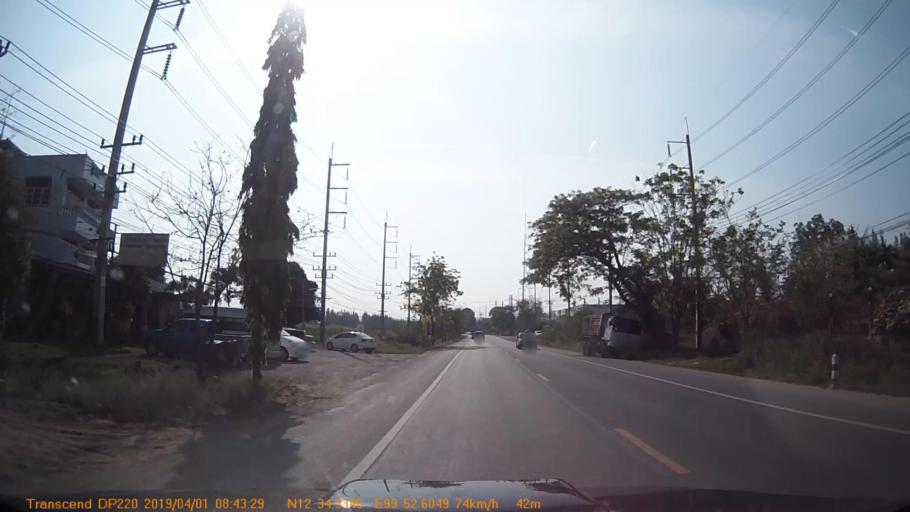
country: TH
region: Prachuap Khiri Khan
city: Hua Hin
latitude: 12.5721
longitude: 99.8771
